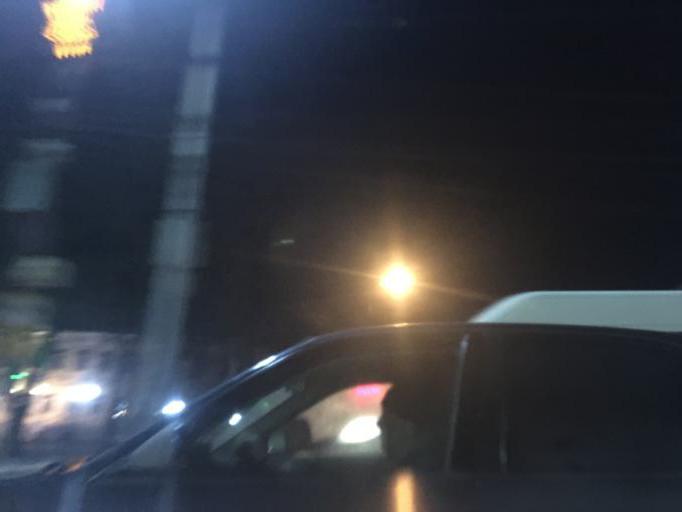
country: RU
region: Tula
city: Tula
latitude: 54.1874
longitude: 37.6112
